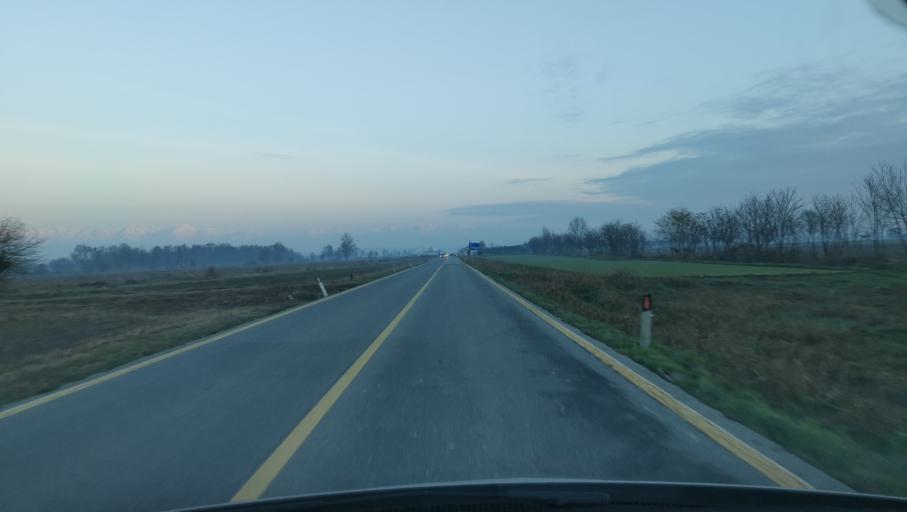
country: IT
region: Piedmont
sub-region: Provincia di Torino
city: Montanaro
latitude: 45.2338
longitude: 7.8911
